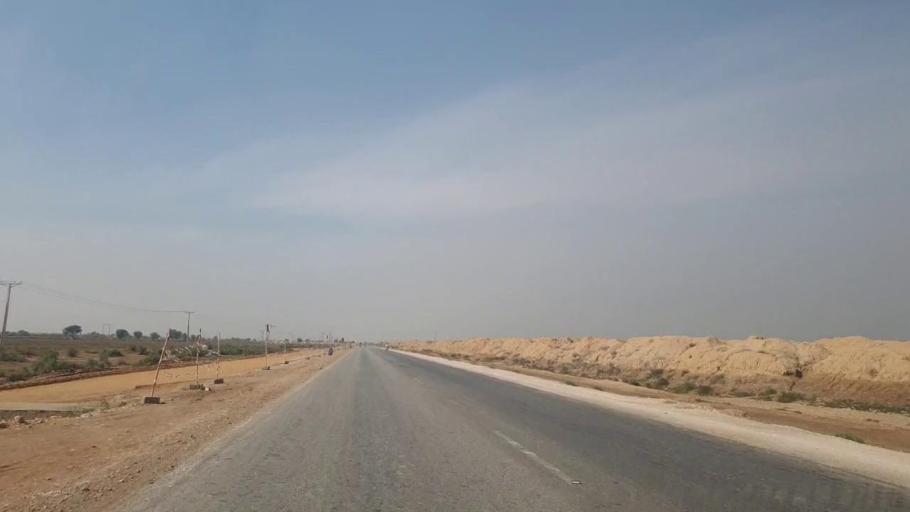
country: PK
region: Sindh
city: Sann
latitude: 26.0049
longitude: 68.1564
